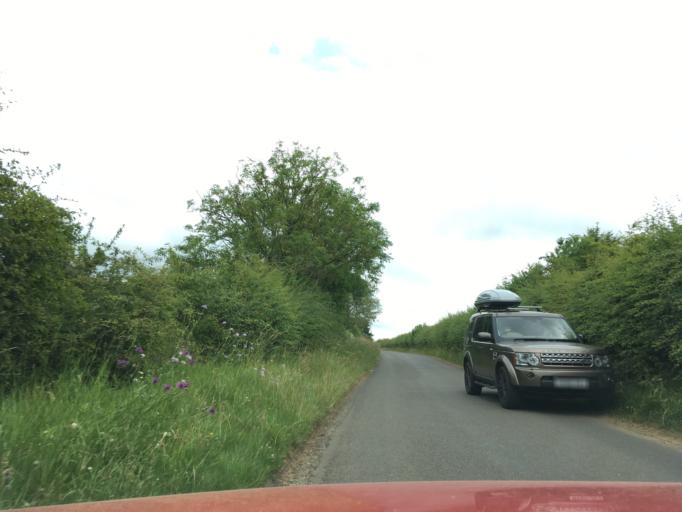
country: GB
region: England
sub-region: Oxfordshire
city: Charlbury
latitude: 51.9339
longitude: -1.4524
